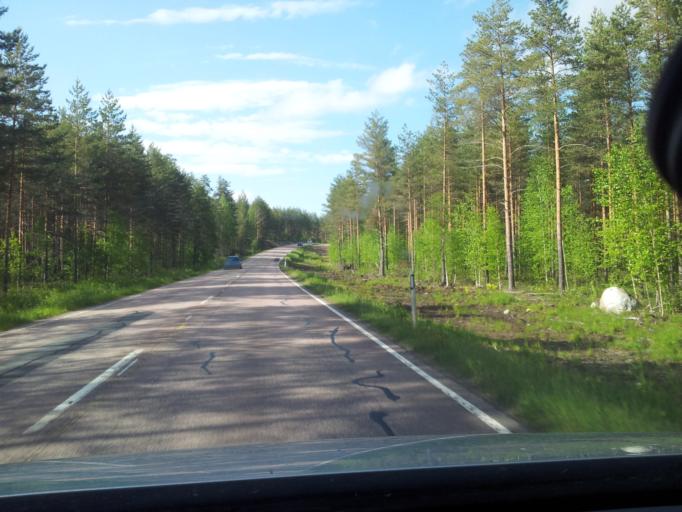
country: FI
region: South Karelia
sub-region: Lappeenranta
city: Luumaeki
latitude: 60.9352
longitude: 27.5831
